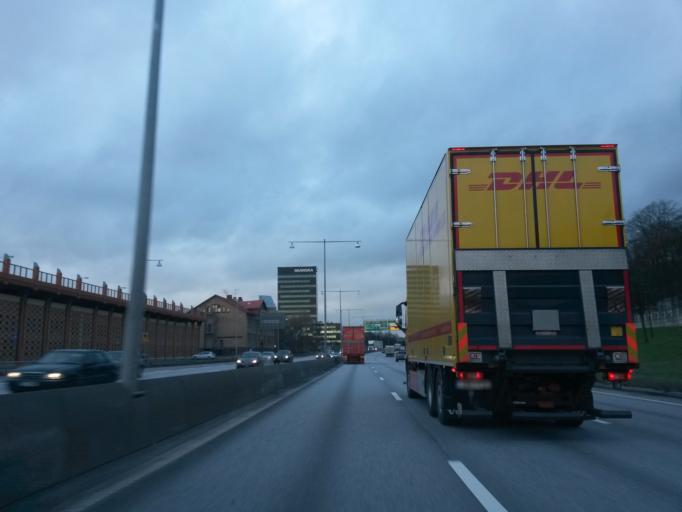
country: SE
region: Vaestra Goetaland
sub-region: Goteborg
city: Goeteborg
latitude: 57.7011
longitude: 11.9951
